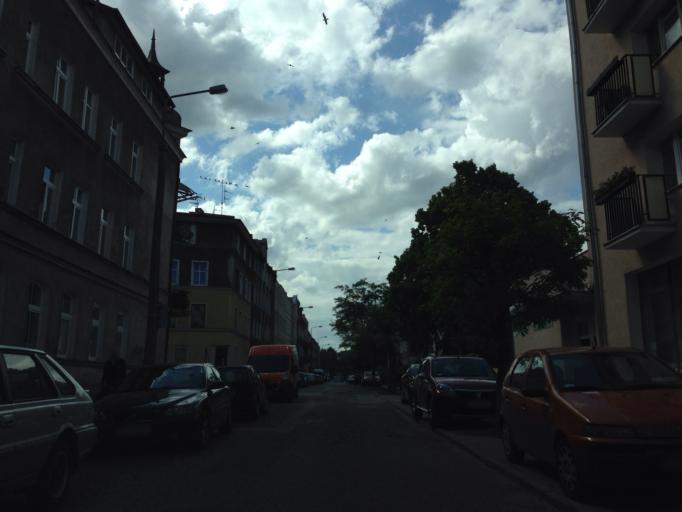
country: PL
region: Pomeranian Voivodeship
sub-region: Gdansk
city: Gdansk
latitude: 54.3833
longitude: 18.6134
